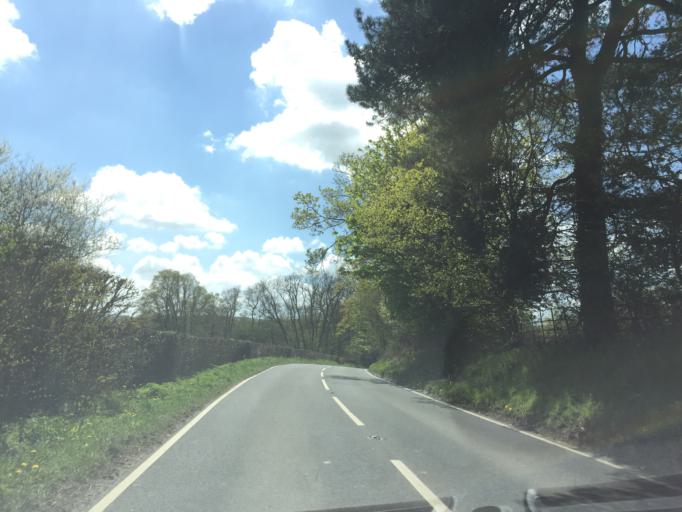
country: GB
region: England
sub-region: East Sussex
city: Crowborough
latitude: 51.1117
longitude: 0.1132
